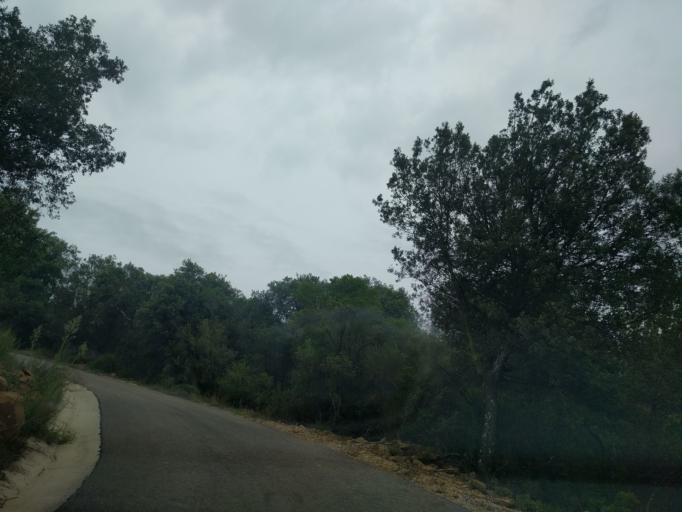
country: ES
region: Catalonia
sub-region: Provincia de Girona
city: la Cellera de Ter
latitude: 42.0221
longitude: 2.6284
